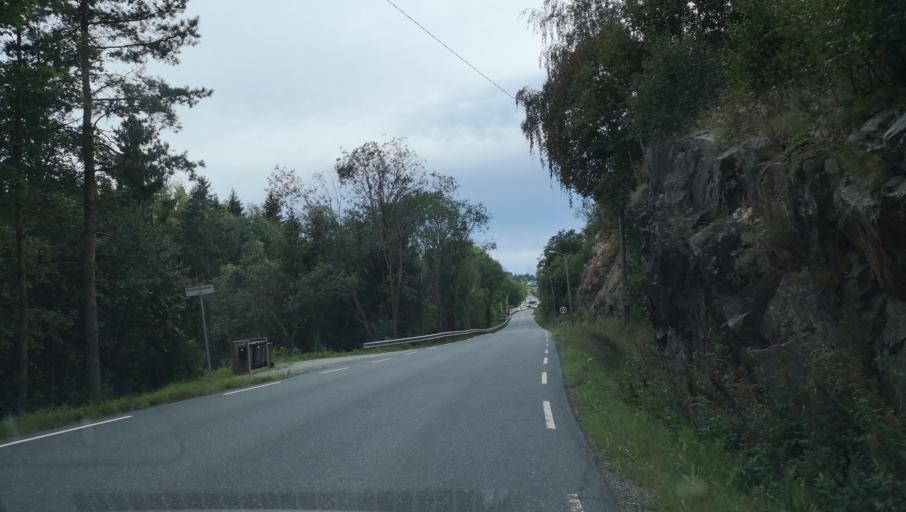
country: NO
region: Ostfold
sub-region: Hobol
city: Tomter
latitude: 59.6675
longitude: 11.0120
